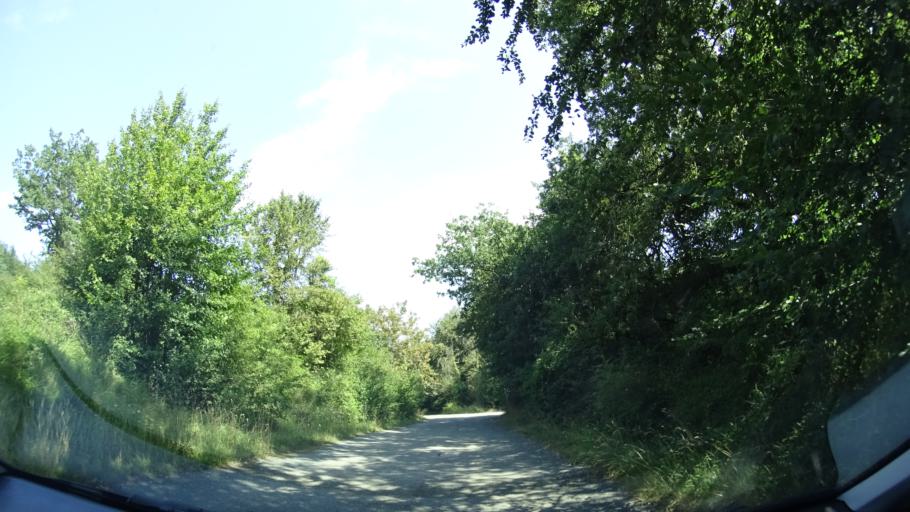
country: ES
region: Basque Country
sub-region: Provincia de Alava
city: Lezama
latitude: 42.9704
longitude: -2.9118
